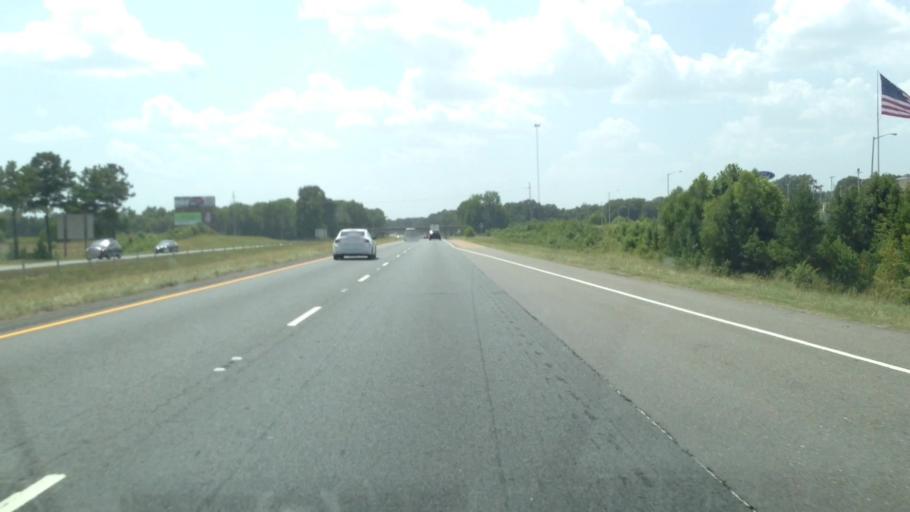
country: US
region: Louisiana
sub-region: Bienville Parish
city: Arcadia
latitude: 32.5647
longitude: -92.9153
